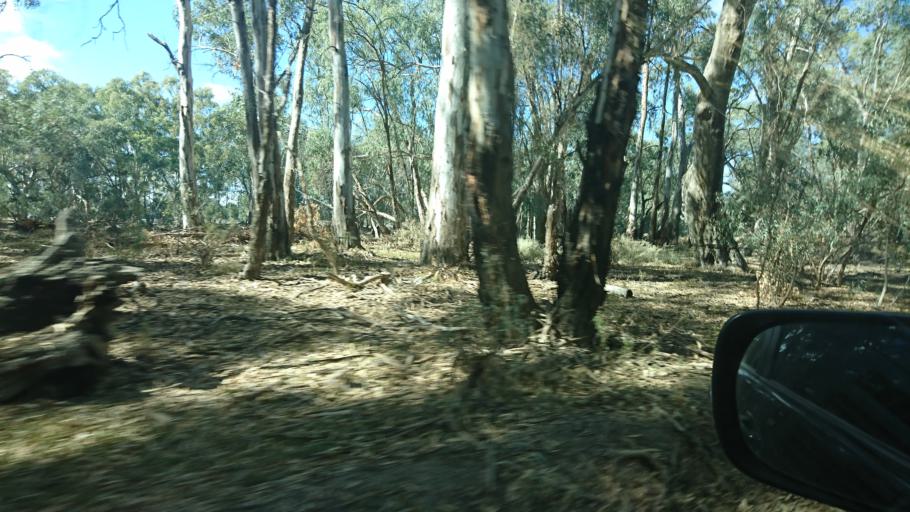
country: AU
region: Victoria
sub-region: Swan Hill
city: Swan Hill
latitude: -35.1402
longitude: 143.3864
